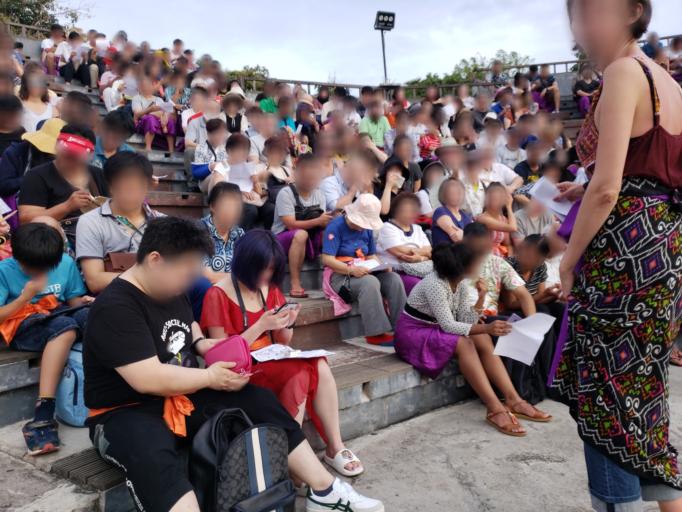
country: ID
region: Bali
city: Pecatu
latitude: -8.8306
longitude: 115.0855
